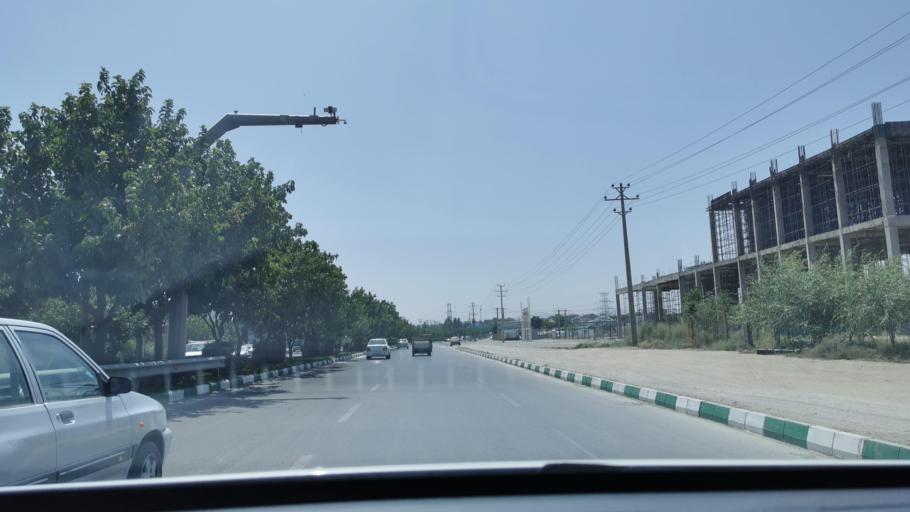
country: IR
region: Razavi Khorasan
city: Mashhad
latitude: 36.3540
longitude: 59.6309
